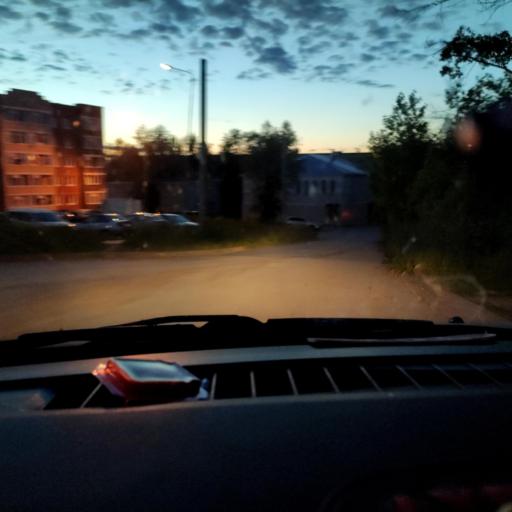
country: RU
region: Perm
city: Lobanovo
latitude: 57.8609
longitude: 56.2896
